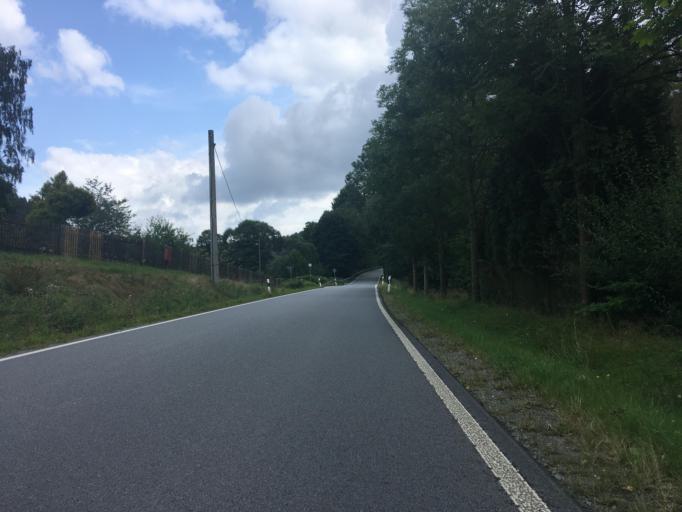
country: CZ
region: Ustecky
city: Mikulasovice
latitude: 50.9279
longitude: 14.3312
